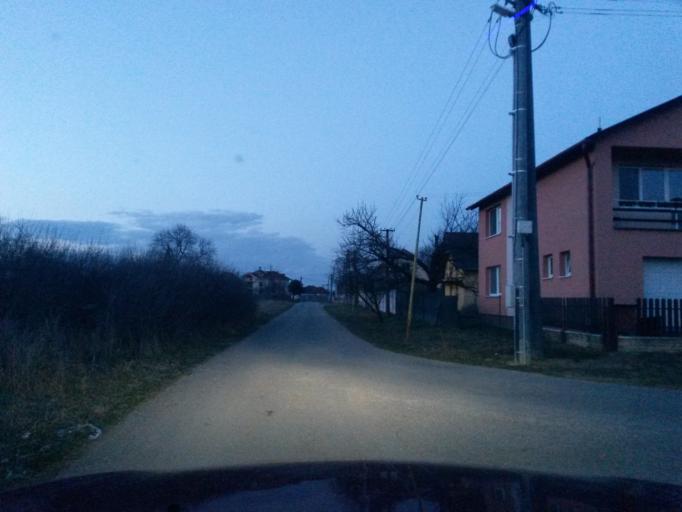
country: SK
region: Kosicky
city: Kosice
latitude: 48.7058
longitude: 21.3299
